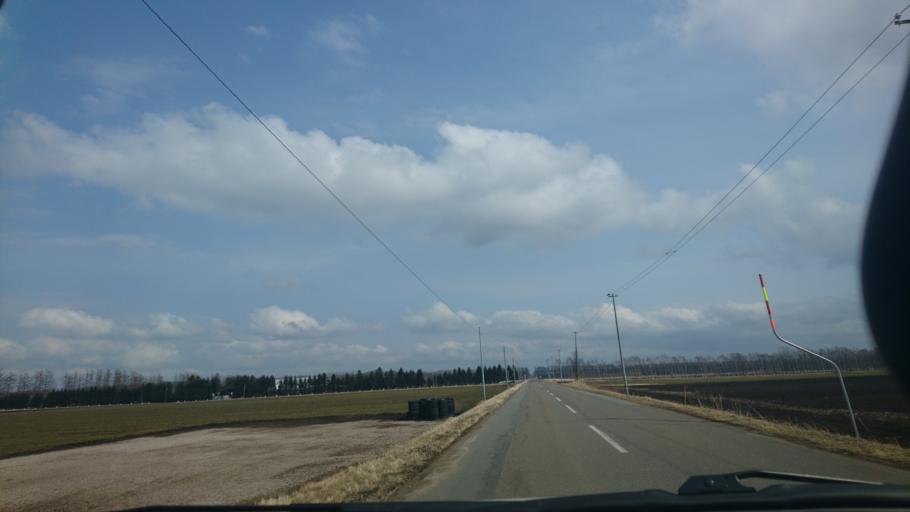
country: JP
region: Hokkaido
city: Otofuke
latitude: 43.2064
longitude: 143.2787
